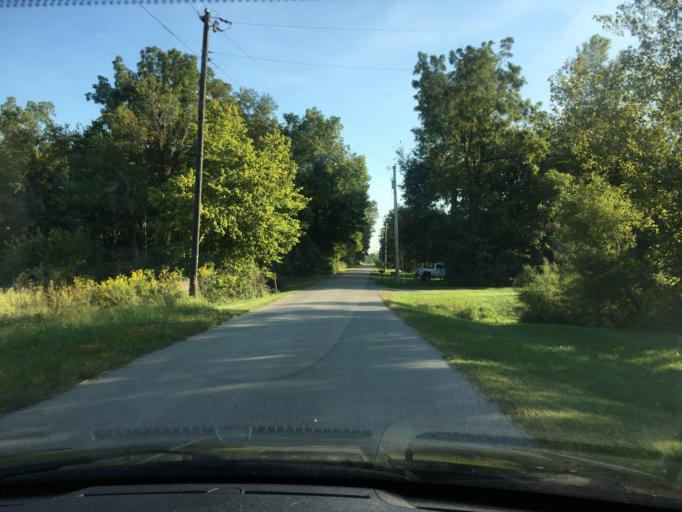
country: US
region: Ohio
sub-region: Logan County
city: West Liberty
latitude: 40.2430
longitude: -83.6678
